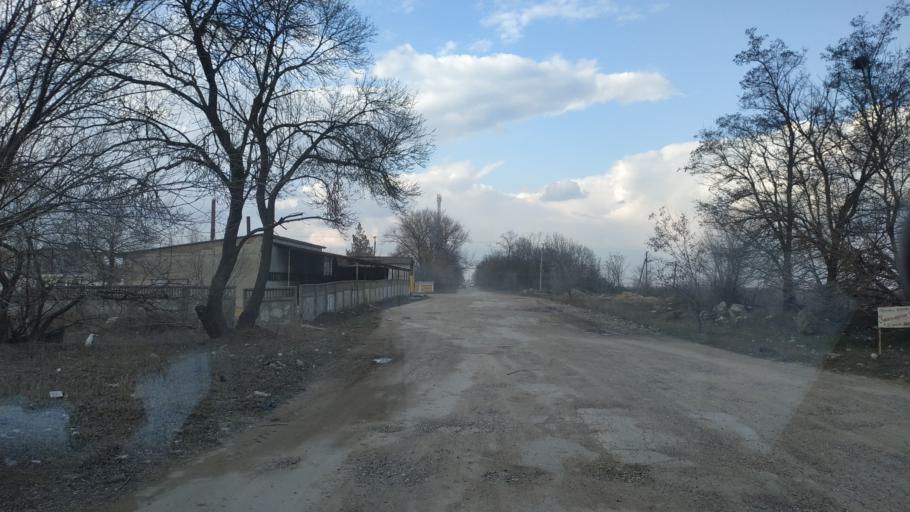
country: MD
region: Anenii Noi
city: Varnita
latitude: 46.8978
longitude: 29.4598
